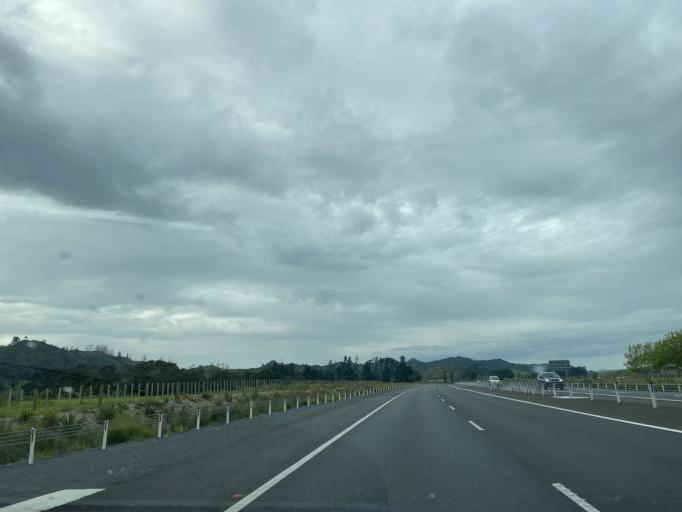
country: NZ
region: Waikato
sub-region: Waikato District
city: Ngaruawahia
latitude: -37.6106
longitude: 175.2046
